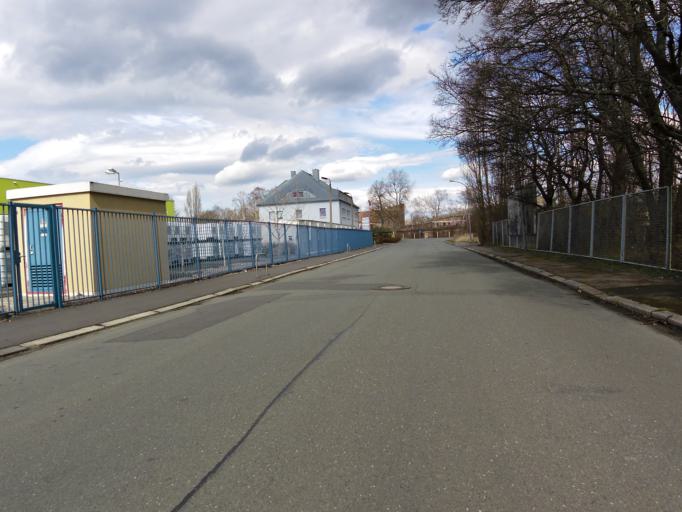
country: DE
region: Saxony
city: Taucha
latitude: 51.3385
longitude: 12.4605
